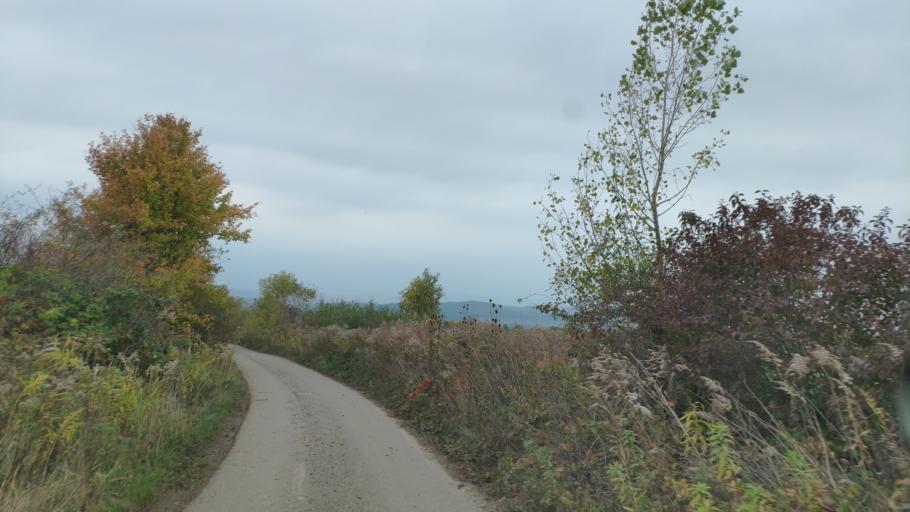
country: SK
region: Kosicky
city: Kosice
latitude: 48.6290
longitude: 21.4053
